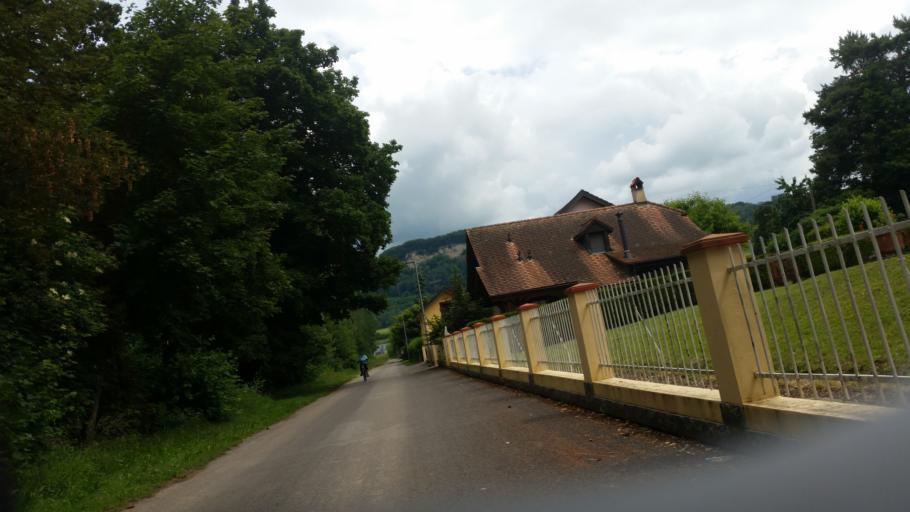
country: CH
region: Vaud
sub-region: Jura-Nord vaudois District
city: Yvonand
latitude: 46.8016
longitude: 6.7467
